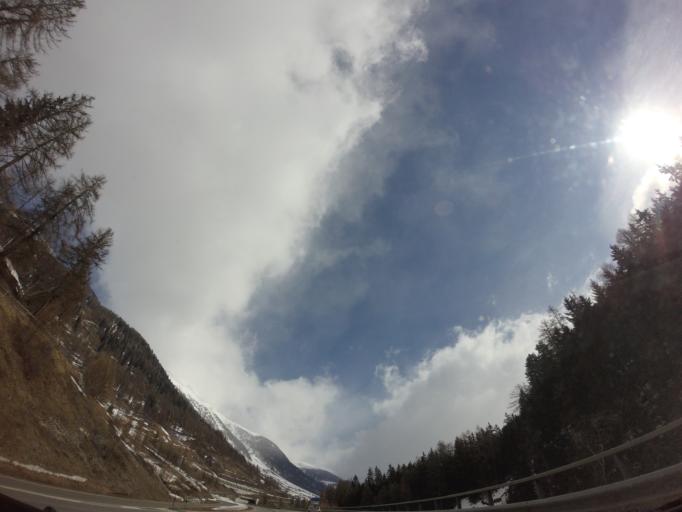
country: CH
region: Grisons
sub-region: Inn District
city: Zernez
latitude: 46.7610
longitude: 10.0937
